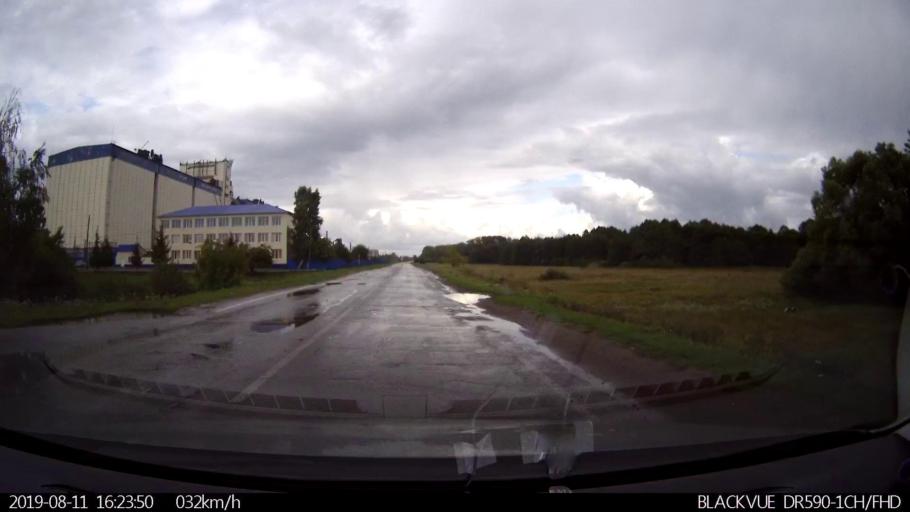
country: RU
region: Ulyanovsk
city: Mayna
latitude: 54.0974
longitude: 47.5896
